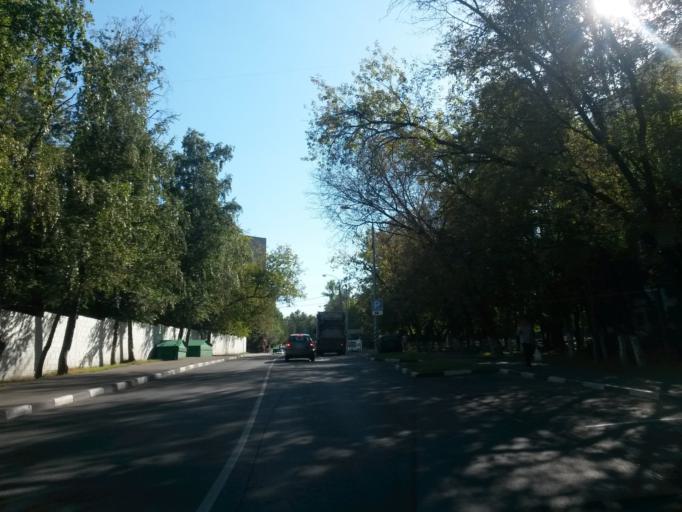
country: RU
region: Moscow
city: Zyuzino
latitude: 55.6540
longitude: 37.5819
